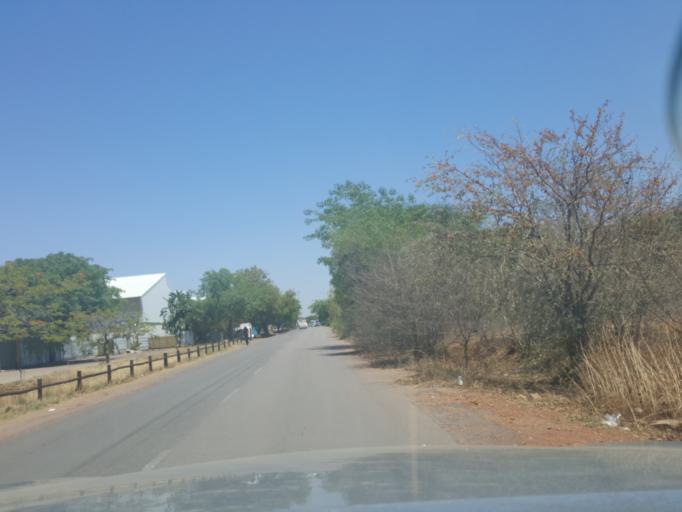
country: BW
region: South East
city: Gaborone
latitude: -24.6857
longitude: 25.8886
